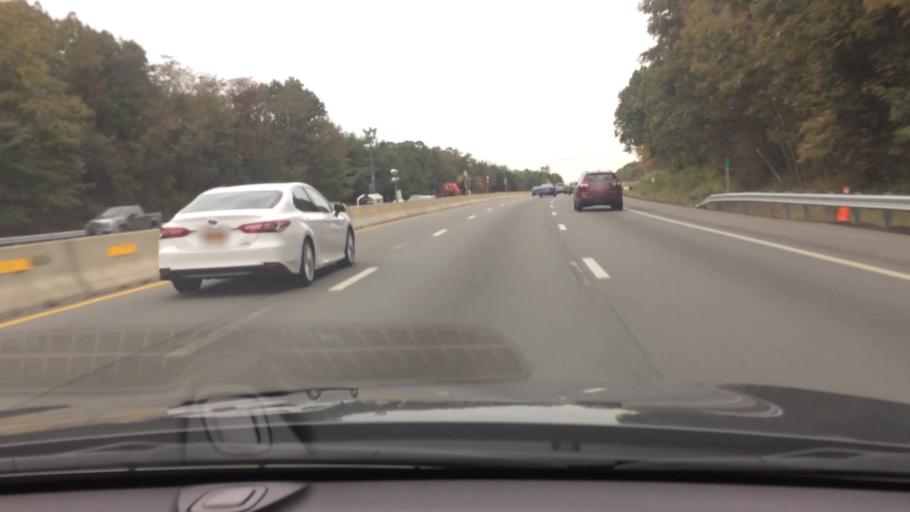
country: US
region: New York
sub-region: Rockland County
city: Monsey
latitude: 41.1057
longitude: -74.0802
